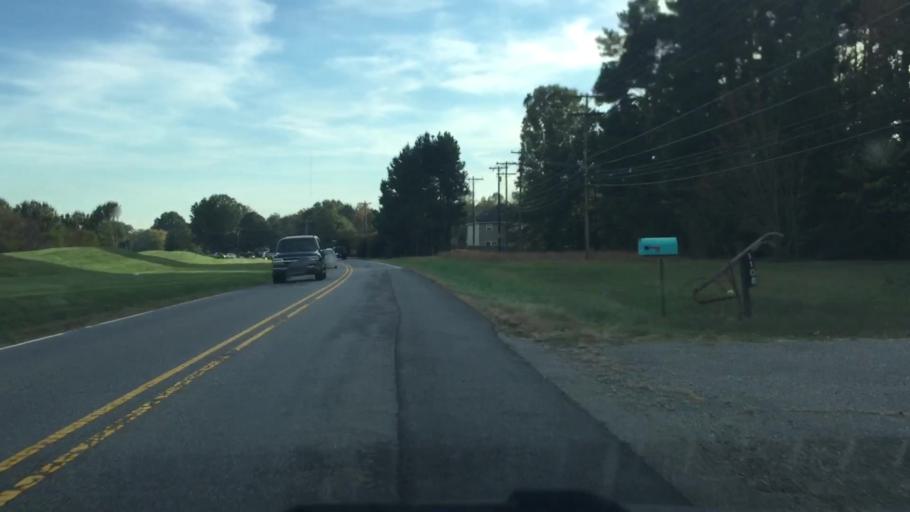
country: US
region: North Carolina
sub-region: Iredell County
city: Mooresville
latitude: 35.5710
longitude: -80.7922
